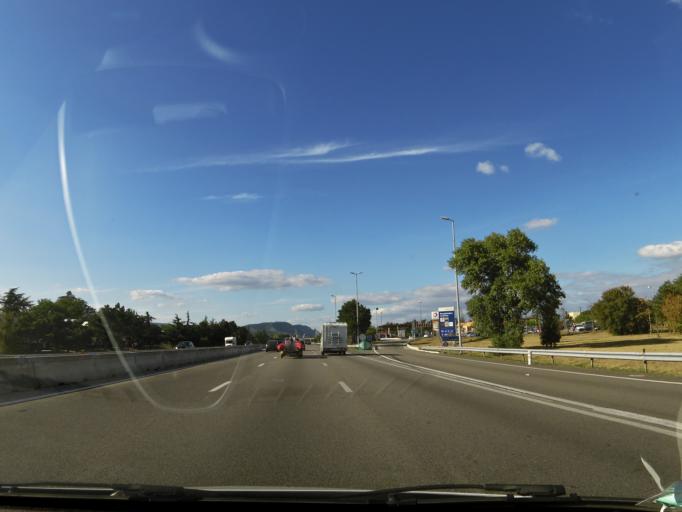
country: FR
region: Rhone-Alpes
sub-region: Departement de la Drome
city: Portes-les-Valence
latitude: 44.8637
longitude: 4.8664
